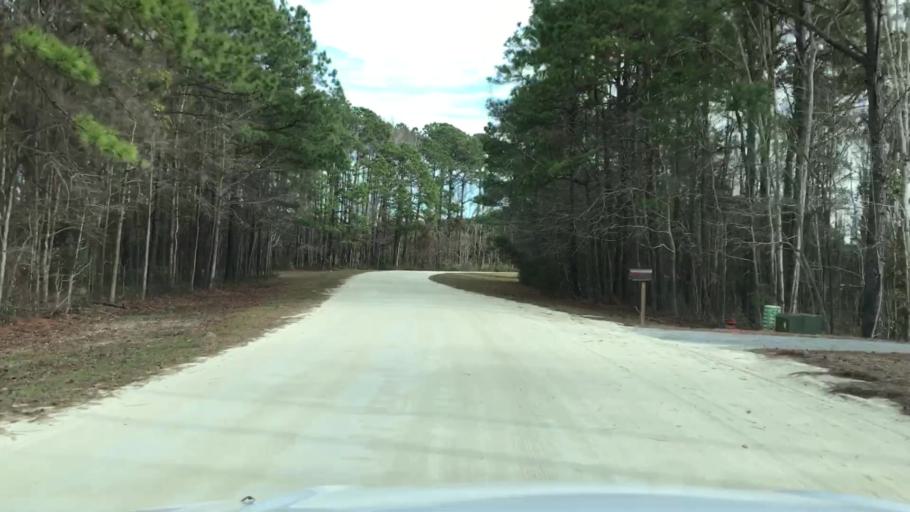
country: US
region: South Carolina
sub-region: Charleston County
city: Isle of Palms
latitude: 32.9030
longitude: -79.7244
